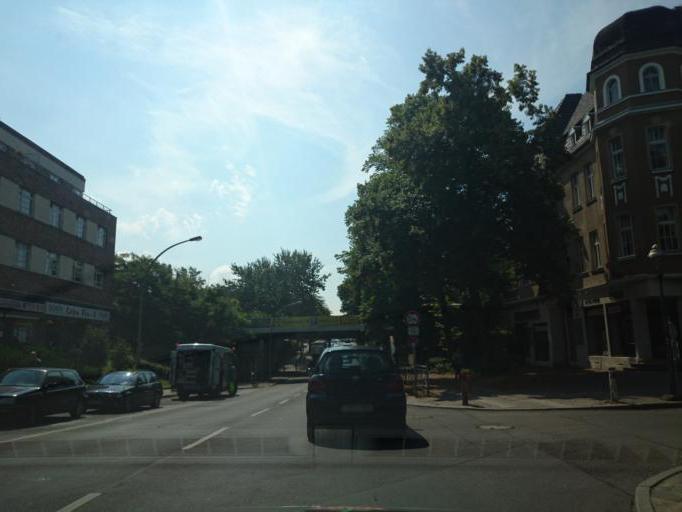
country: DE
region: Berlin
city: Dahlem
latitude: 52.4444
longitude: 13.2950
